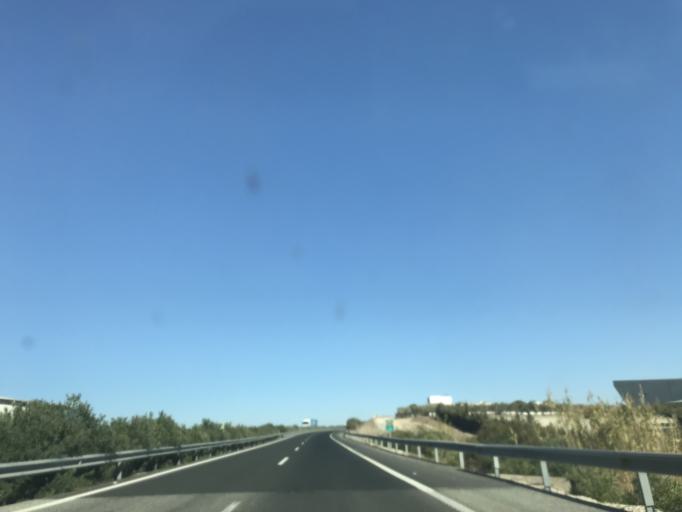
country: ES
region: Andalusia
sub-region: Provincia de Sevilla
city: La Puebla de Cazalla
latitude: 37.2255
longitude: -5.2896
